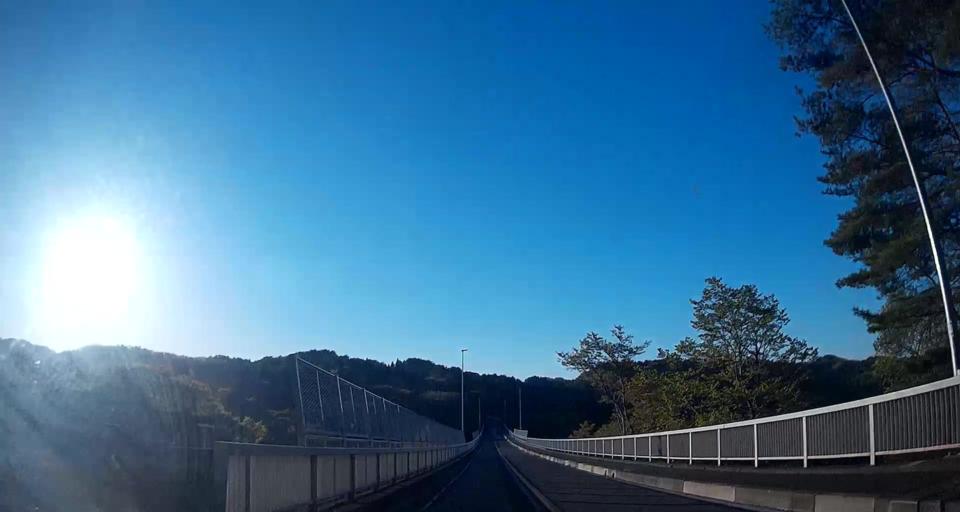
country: JP
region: Iwate
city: Miyako
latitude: 39.6503
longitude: 141.9710
